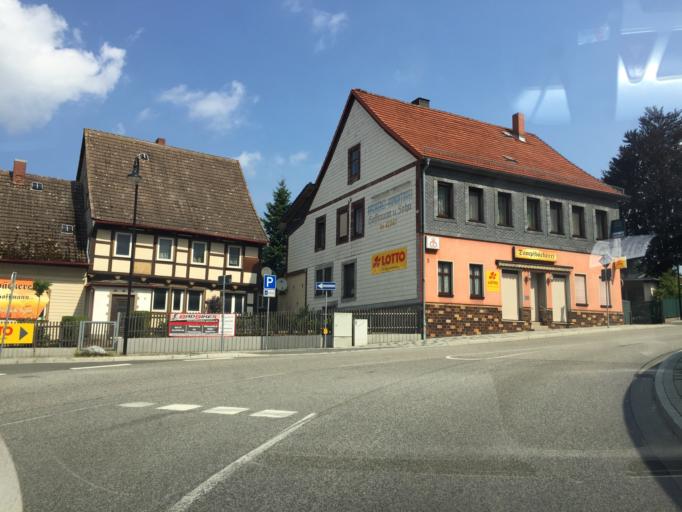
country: DE
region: Saxony-Anhalt
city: Elbingerode
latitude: 51.7728
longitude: 10.8034
